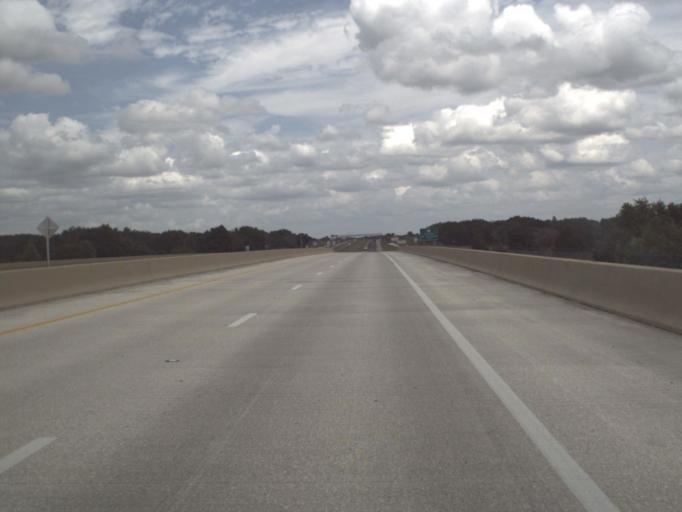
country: US
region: Florida
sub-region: Lake County
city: Mount Plymouth
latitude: 28.7911
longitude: -81.5184
